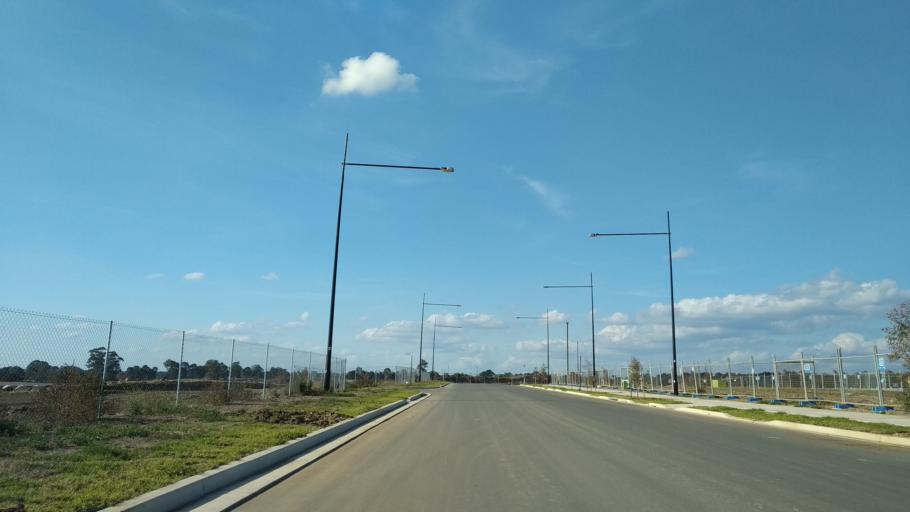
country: AU
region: New South Wales
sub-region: Blacktown
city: Hassall Grove
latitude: -33.6888
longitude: 150.8150
